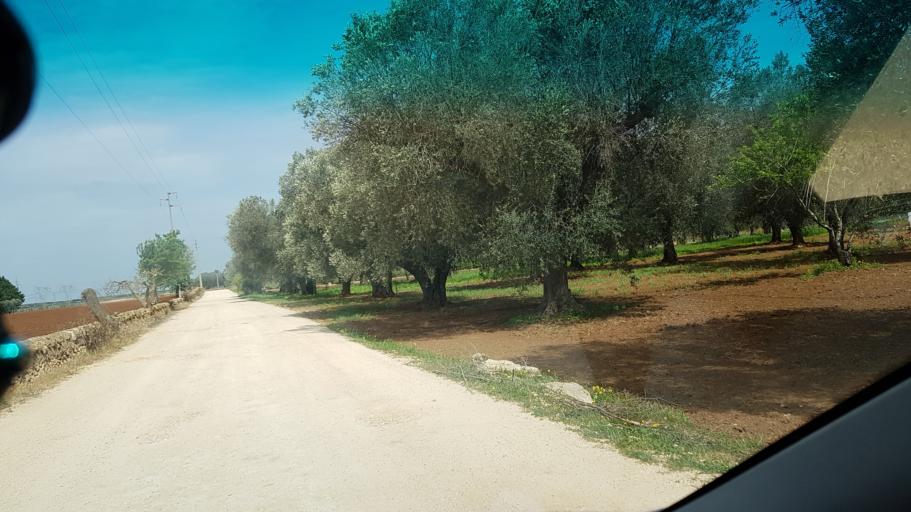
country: IT
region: Apulia
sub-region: Provincia di Brindisi
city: Mesagne
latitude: 40.6004
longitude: 17.8542
